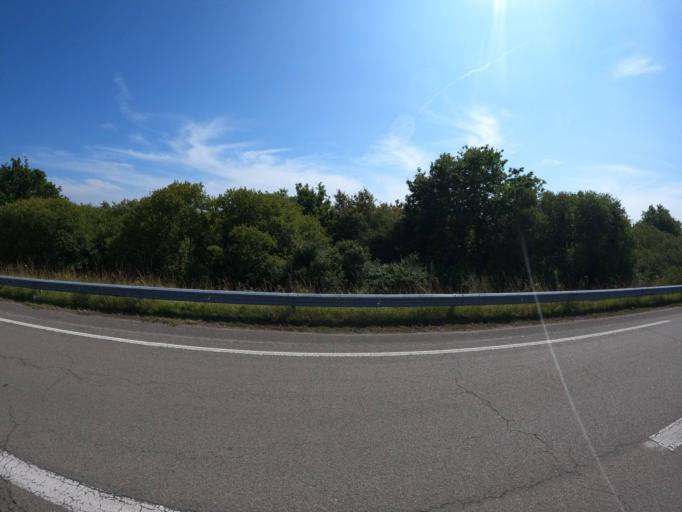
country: FR
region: Pays de la Loire
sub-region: Departement de la Loire-Atlantique
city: La Bernerie-en-Retz
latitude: 47.1040
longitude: -2.0467
